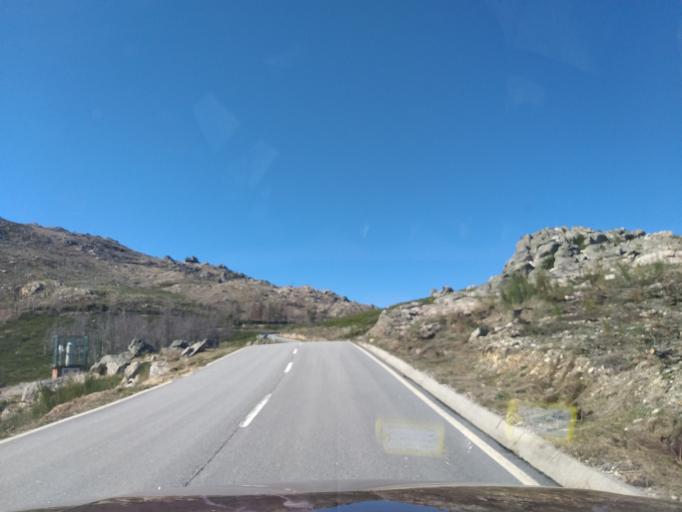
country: PT
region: Guarda
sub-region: Manteigas
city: Manteigas
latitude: 40.4794
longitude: -7.5118
